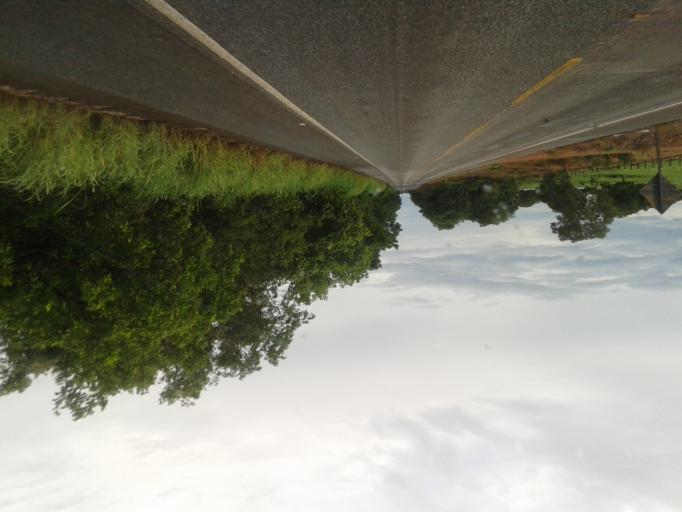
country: BR
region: Goias
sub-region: Mozarlandia
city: Mozarlandia
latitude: -14.8601
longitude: -50.5467
